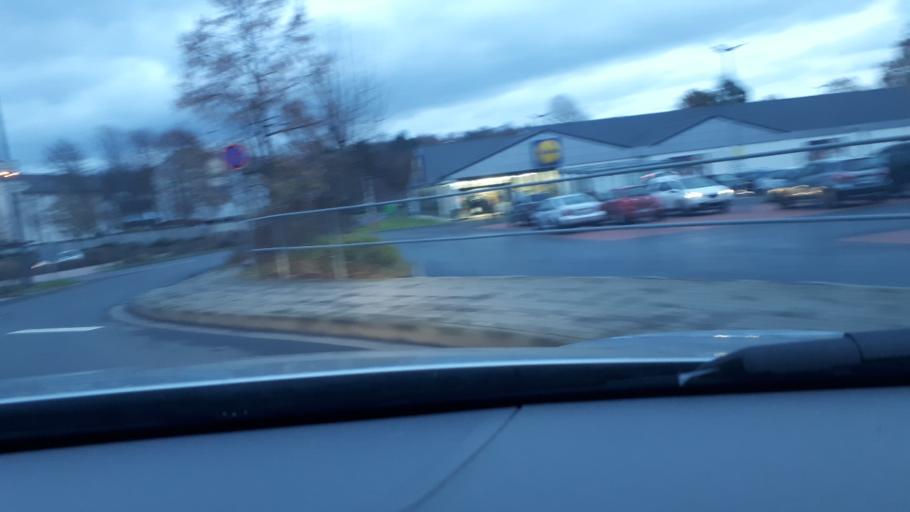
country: DE
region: Rheinland-Pfalz
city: Mayen
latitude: 50.3226
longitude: 7.2274
